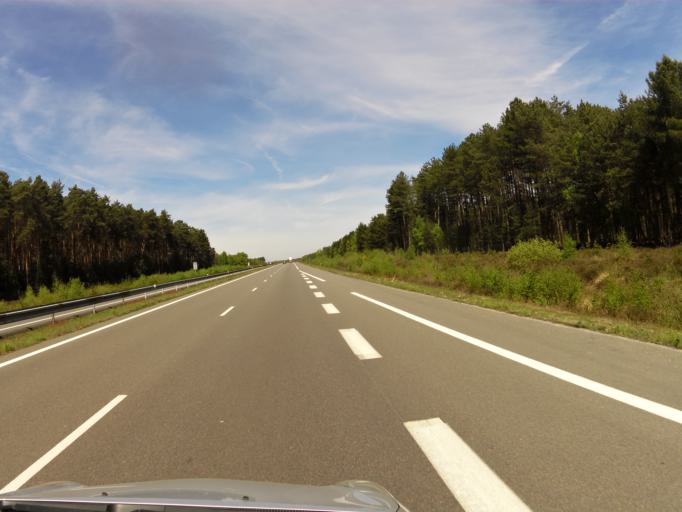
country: FR
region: Centre
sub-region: Departement du Loir-et-Cher
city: Theillay
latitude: 47.3547
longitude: 2.0510
